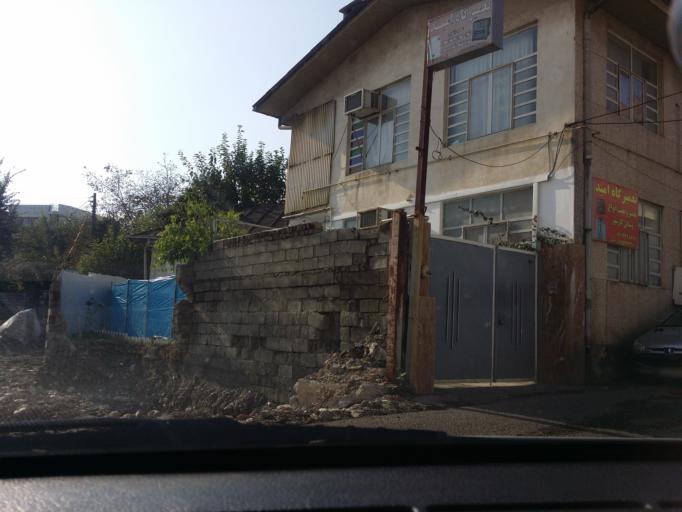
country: IR
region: Mazandaran
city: Chalus
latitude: 36.6552
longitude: 51.4167
